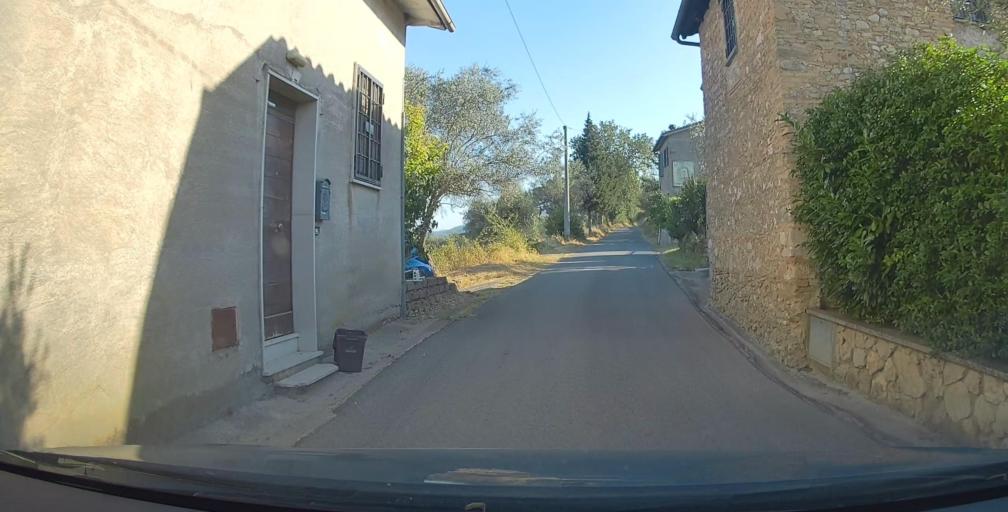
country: IT
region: Umbria
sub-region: Provincia di Terni
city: Calvi dell'Umbria
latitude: 42.3739
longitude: 12.5658
